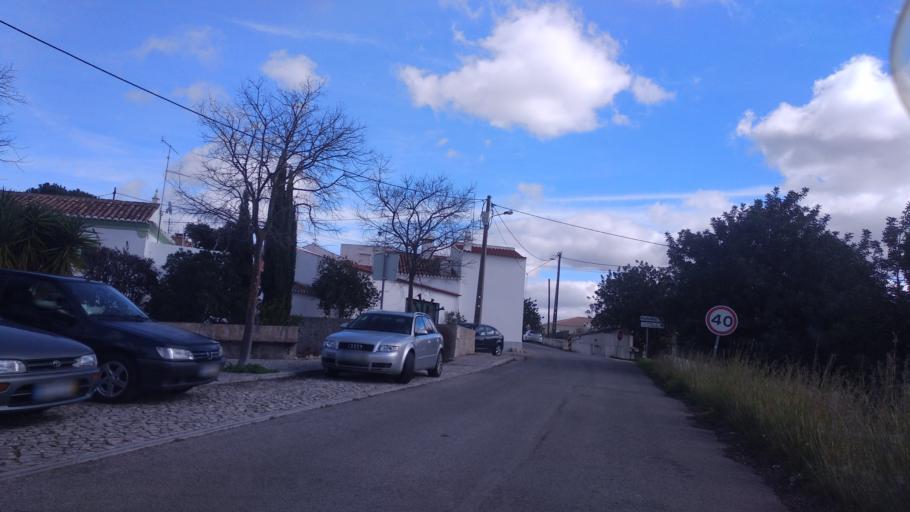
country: PT
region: Faro
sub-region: Sao Bras de Alportel
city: Sao Bras de Alportel
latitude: 37.1493
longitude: -7.8999
